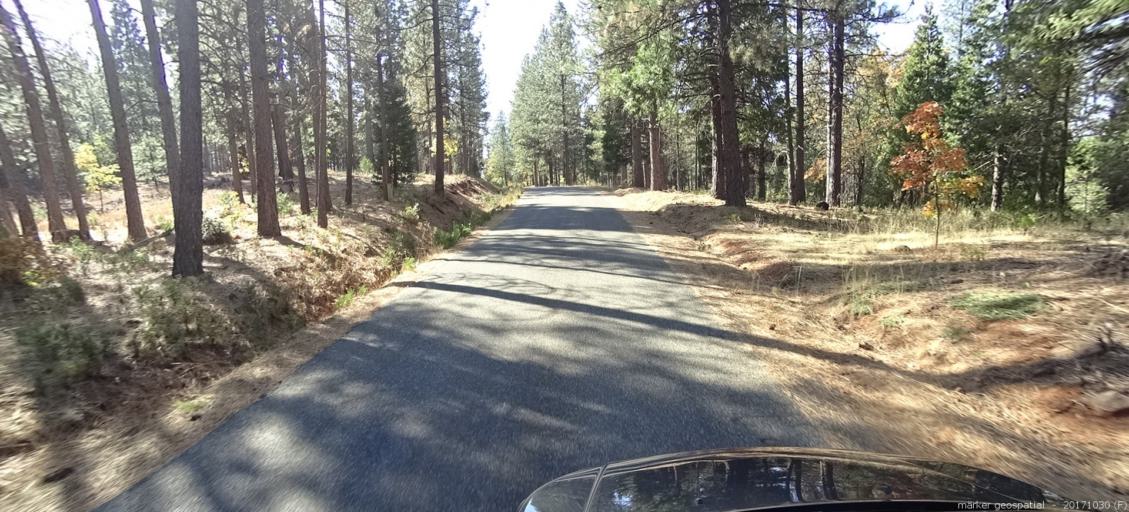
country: US
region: California
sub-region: Shasta County
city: Shingletown
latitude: 40.6003
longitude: -121.8566
